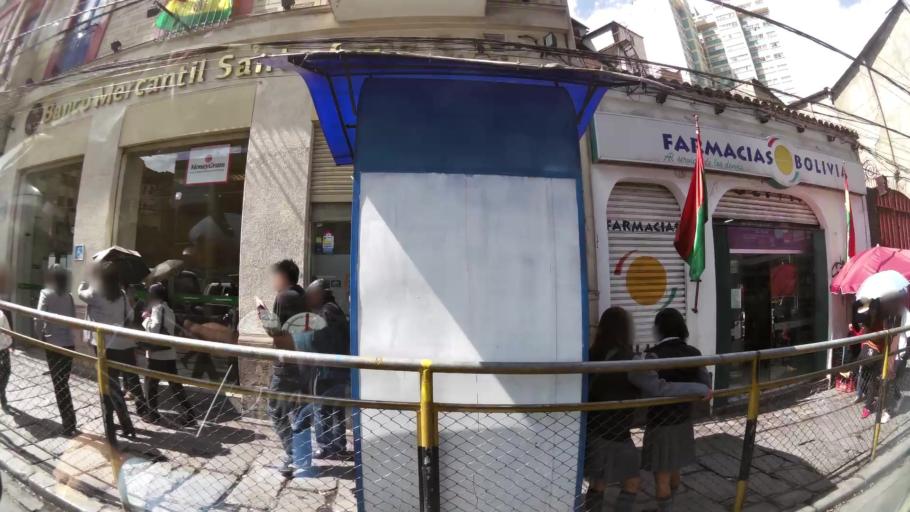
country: BO
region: La Paz
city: La Paz
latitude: -16.4933
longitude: -68.1369
